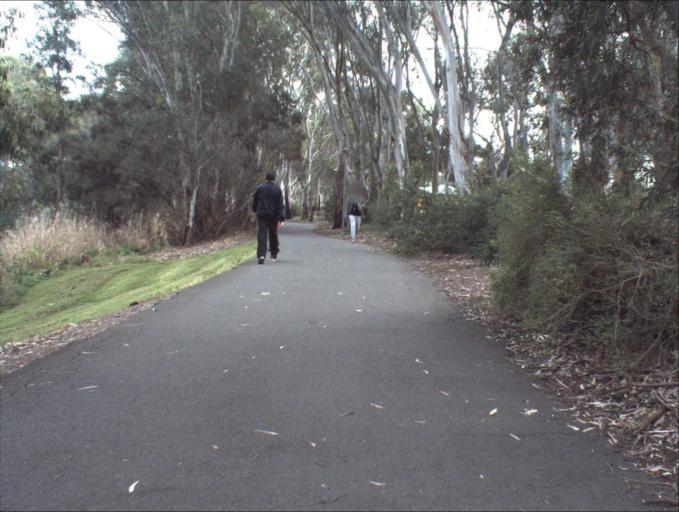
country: AU
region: South Australia
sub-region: Campbelltown
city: Paradise
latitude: -34.8674
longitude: 138.6668
